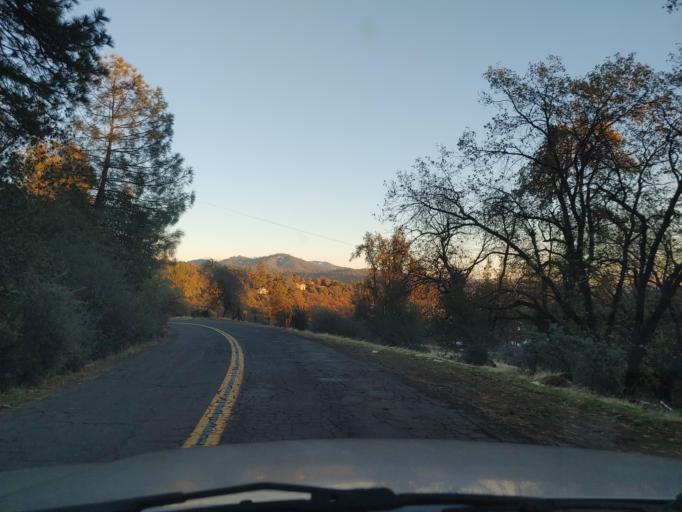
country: US
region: California
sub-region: Tuolumne County
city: Cedar Ridge
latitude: 38.0415
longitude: -120.2863
